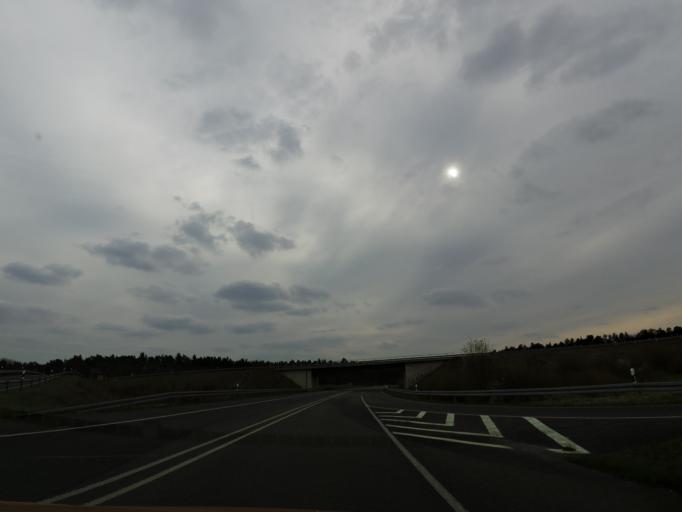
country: DE
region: Brandenburg
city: Mullrose
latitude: 52.2379
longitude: 14.3944
